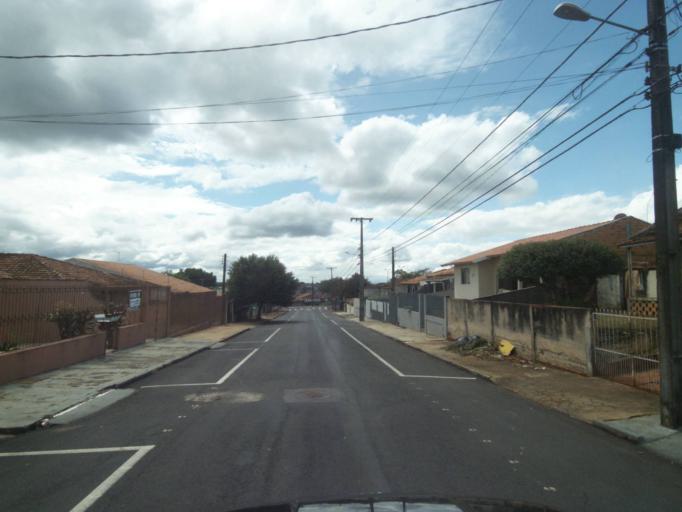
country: BR
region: Parana
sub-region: Telemaco Borba
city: Telemaco Borba
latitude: -24.3199
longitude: -50.6405
